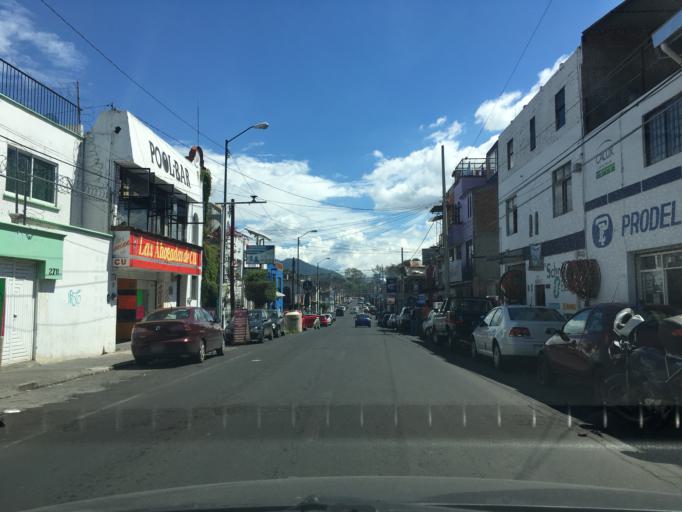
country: MX
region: Michoacan
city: Morelia
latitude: 19.6902
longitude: -101.1990
